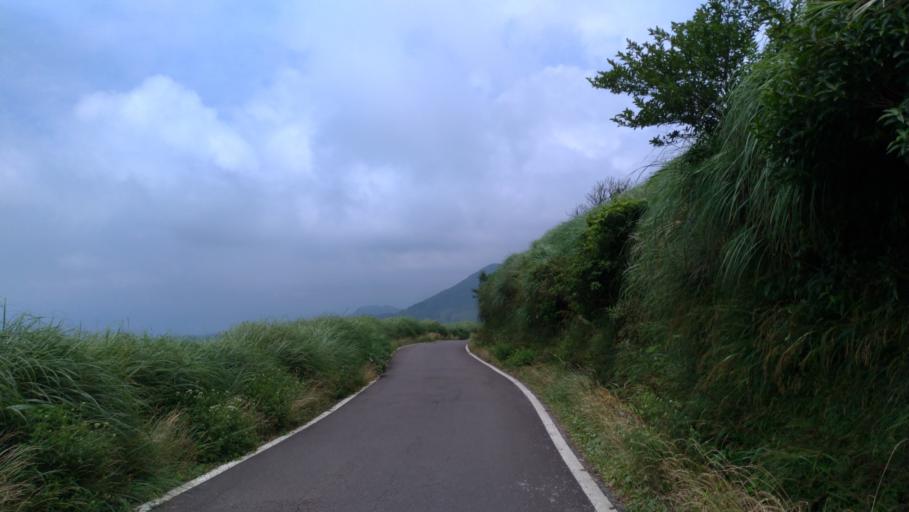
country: TW
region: Taipei
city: Taipei
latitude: 25.1799
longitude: 121.5211
